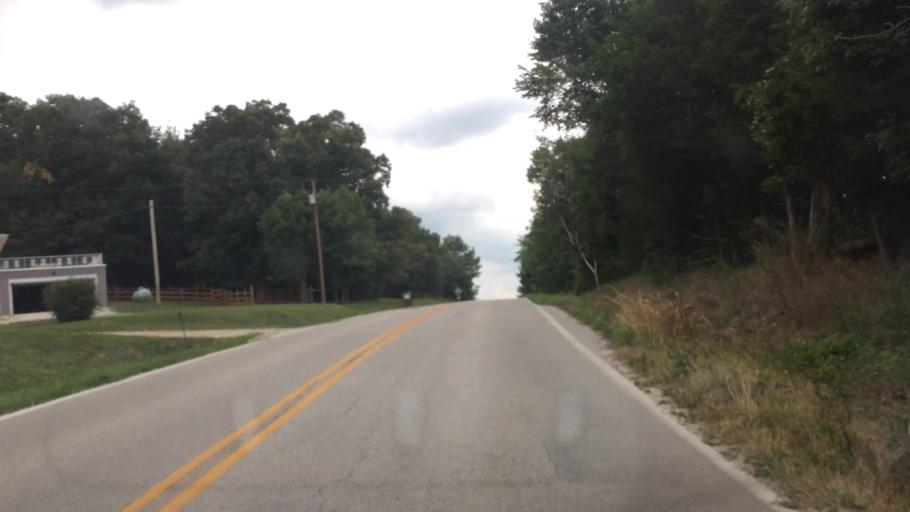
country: US
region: Missouri
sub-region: Greene County
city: Strafford
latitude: 37.2968
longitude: -93.0849
